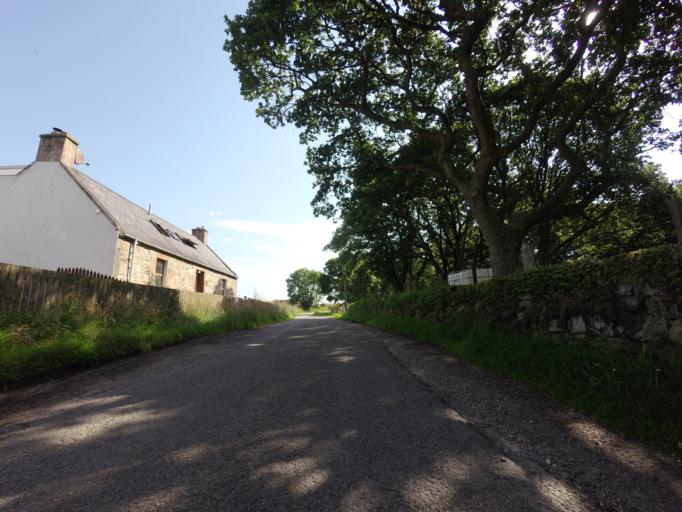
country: GB
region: Scotland
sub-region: Highland
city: Alness
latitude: 57.7090
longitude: -4.2298
